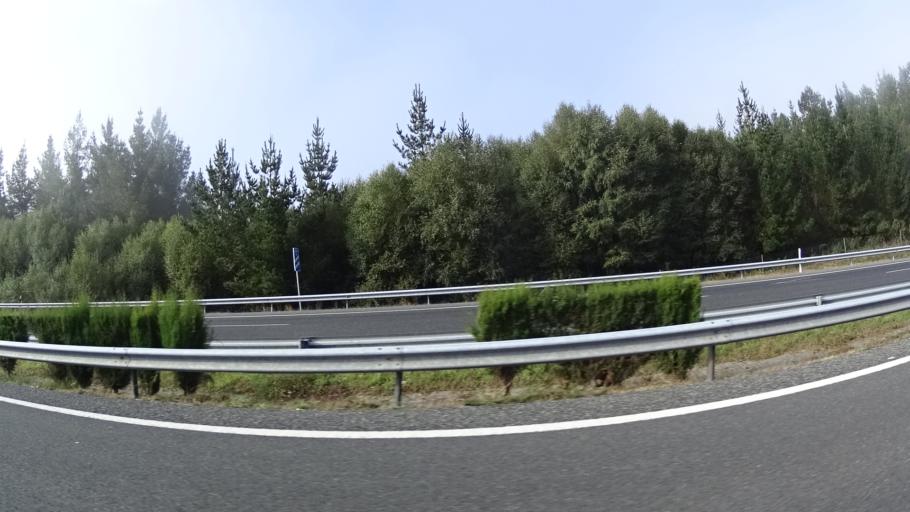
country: ES
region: Galicia
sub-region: Provincia de Lugo
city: Lancara
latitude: 42.9217
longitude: -7.3541
